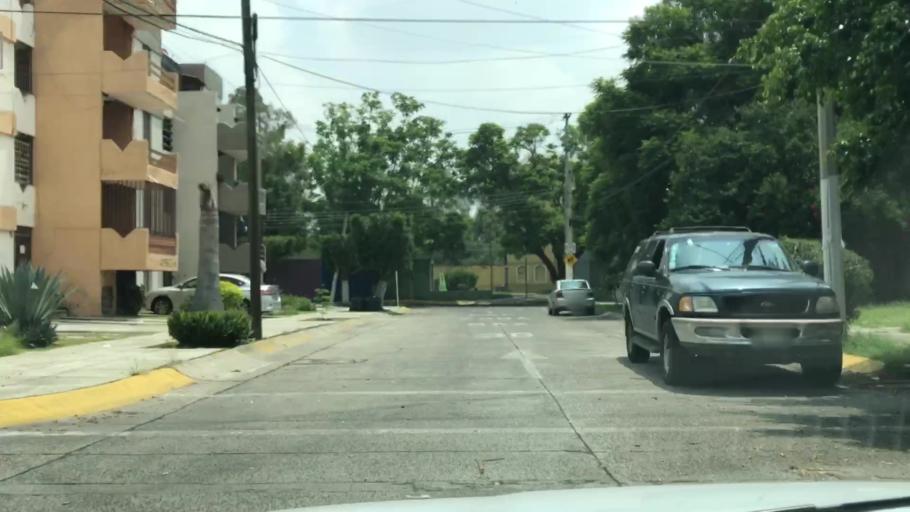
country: MX
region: Jalisco
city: Guadalajara
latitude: 20.6548
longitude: -103.4218
